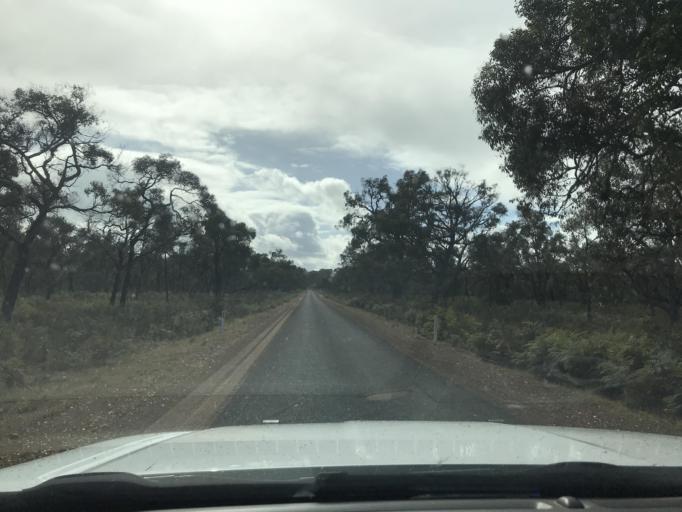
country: AU
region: South Australia
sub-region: Wattle Range
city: Penola
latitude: -37.1890
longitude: 141.2443
